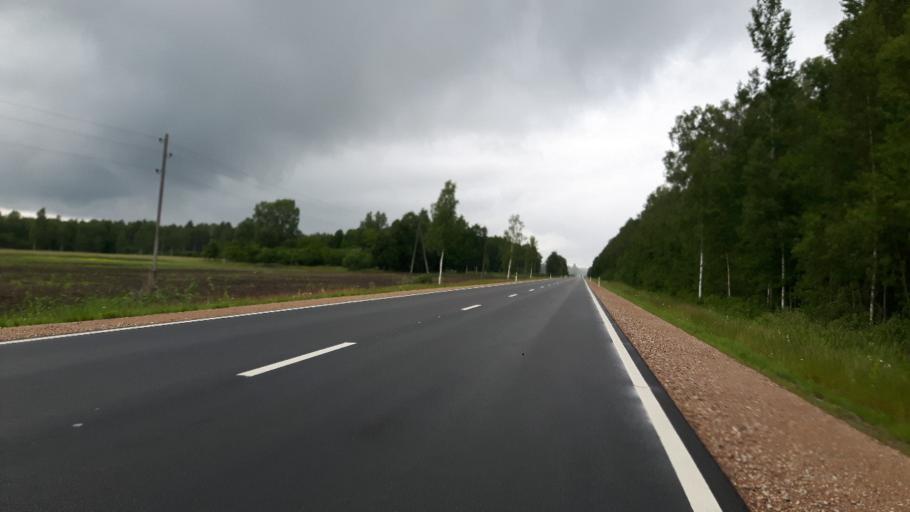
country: LV
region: Nica
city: Nica
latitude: 56.2579
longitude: 21.0960
